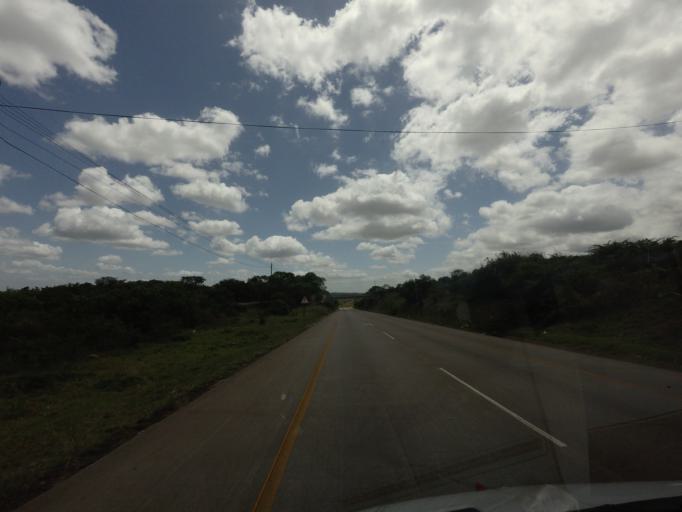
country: ZA
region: KwaZulu-Natal
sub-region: uMkhanyakude District Municipality
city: Mtubatuba
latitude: -28.4630
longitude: 32.1480
